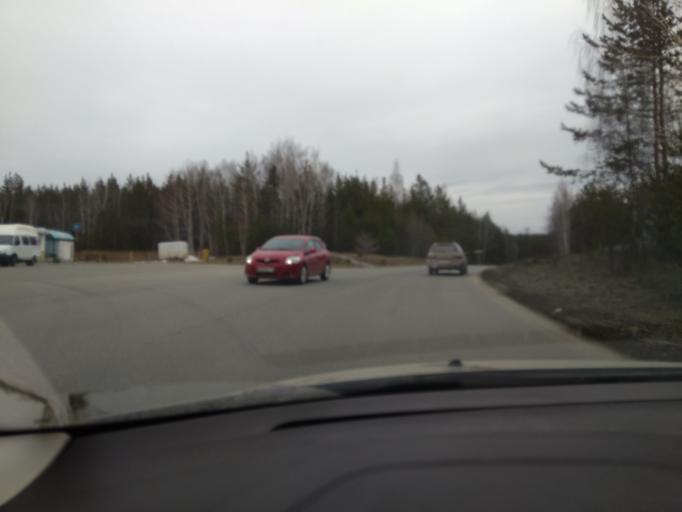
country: RU
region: Chelyabinsk
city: Kyshtym
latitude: 55.7086
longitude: 60.5774
